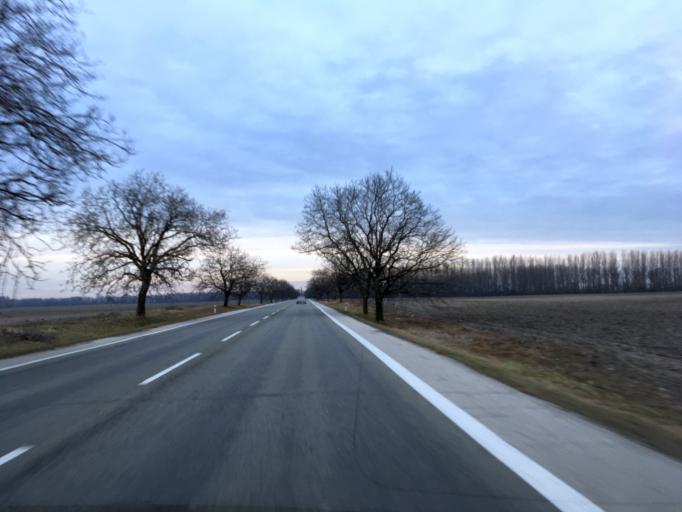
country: SK
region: Trnavsky
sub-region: Okres Dunajska Streda
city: Velky Meder
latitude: 47.9121
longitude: 17.7317
